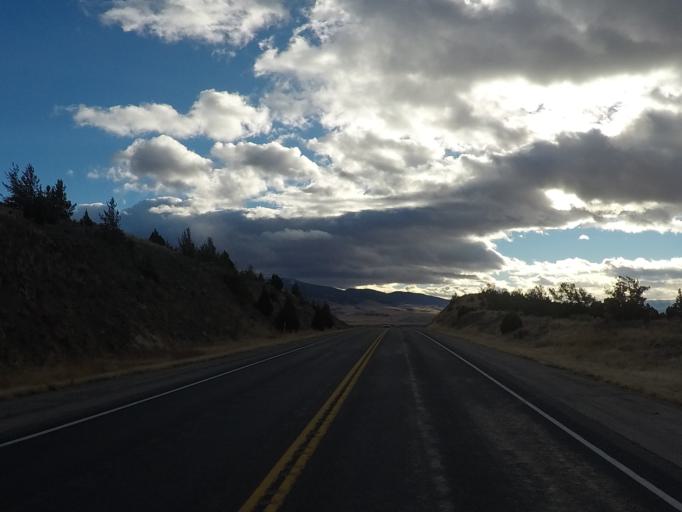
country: US
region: Montana
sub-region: Jefferson County
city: Whitehall
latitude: 45.8906
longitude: -111.9655
